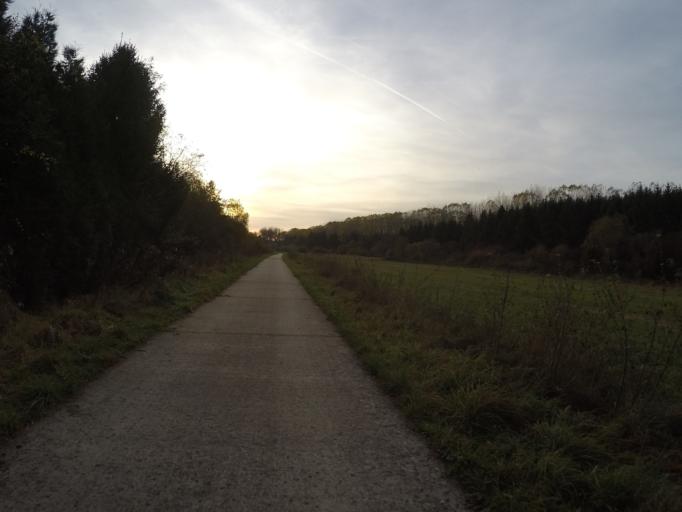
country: BE
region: Wallonia
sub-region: Province du Luxembourg
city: Marche-en-Famenne
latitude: 50.2471
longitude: 5.3838
